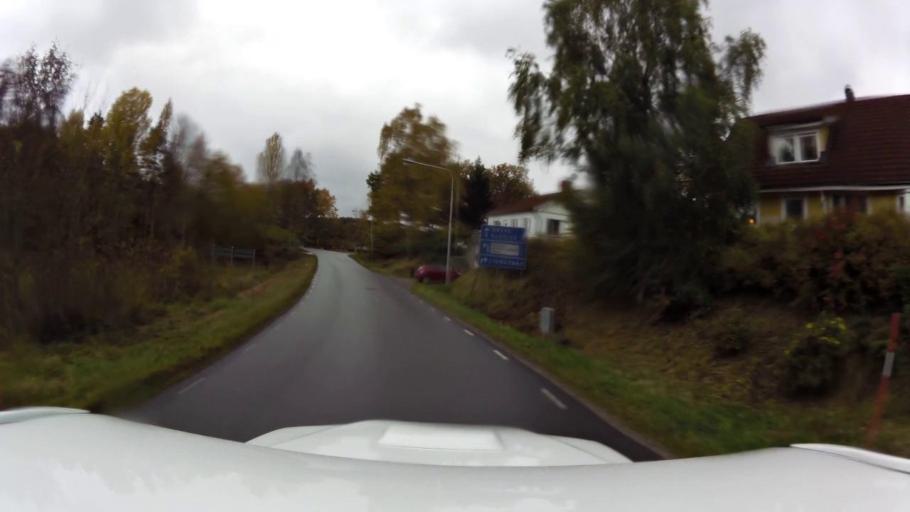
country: SE
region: OEstergoetland
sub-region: Linkopings Kommun
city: Ljungsbro
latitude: 58.5182
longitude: 15.5180
